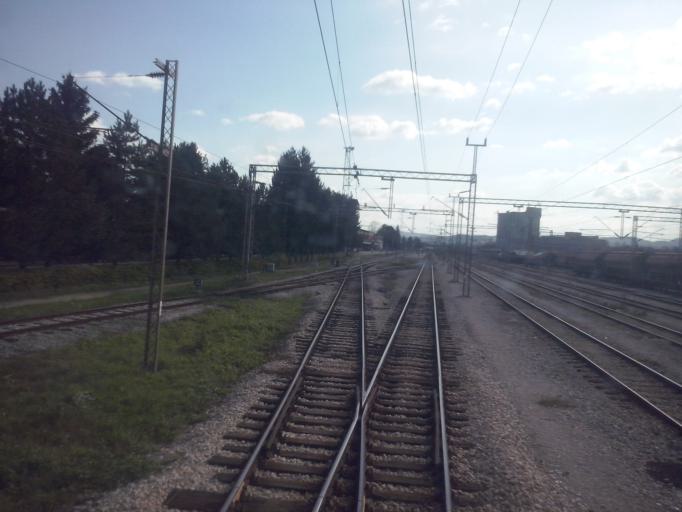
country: RS
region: Central Serbia
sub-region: Zlatiborski Okrug
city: Pozega
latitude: 43.8427
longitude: 20.0261
